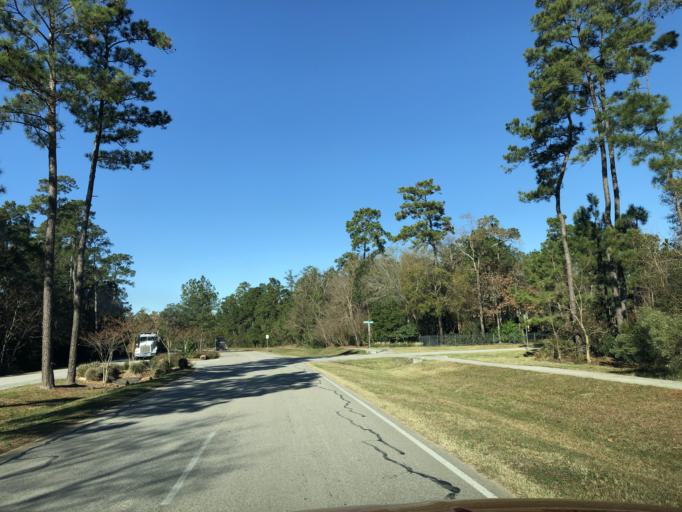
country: US
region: Texas
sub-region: Montgomery County
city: Porter Heights
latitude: 30.0867
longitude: -95.3356
